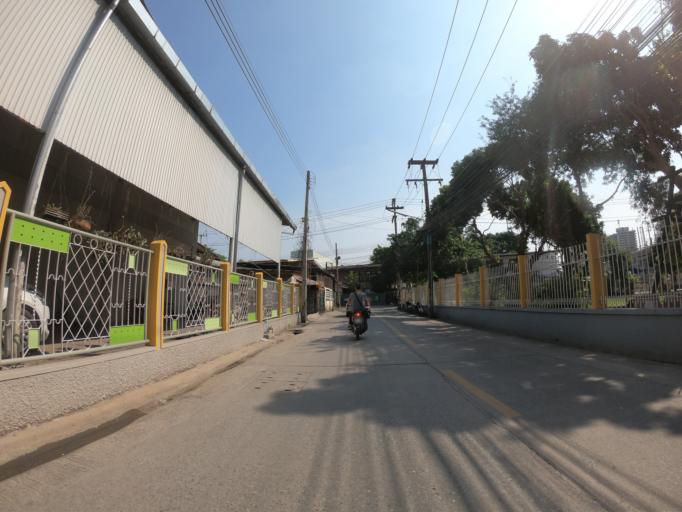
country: TH
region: Chiang Mai
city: Chiang Mai
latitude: 18.7985
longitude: 99.0001
